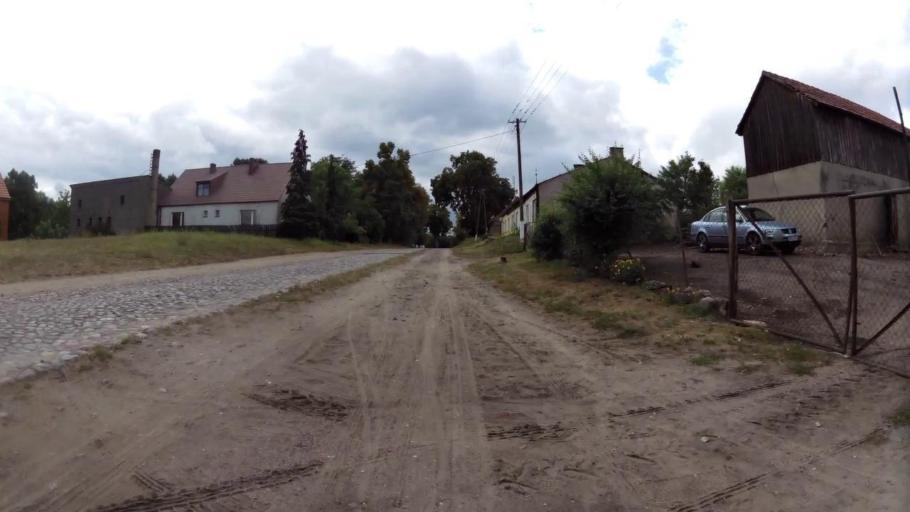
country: PL
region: West Pomeranian Voivodeship
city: Trzcinsko Zdroj
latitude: 52.8854
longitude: 14.7145
